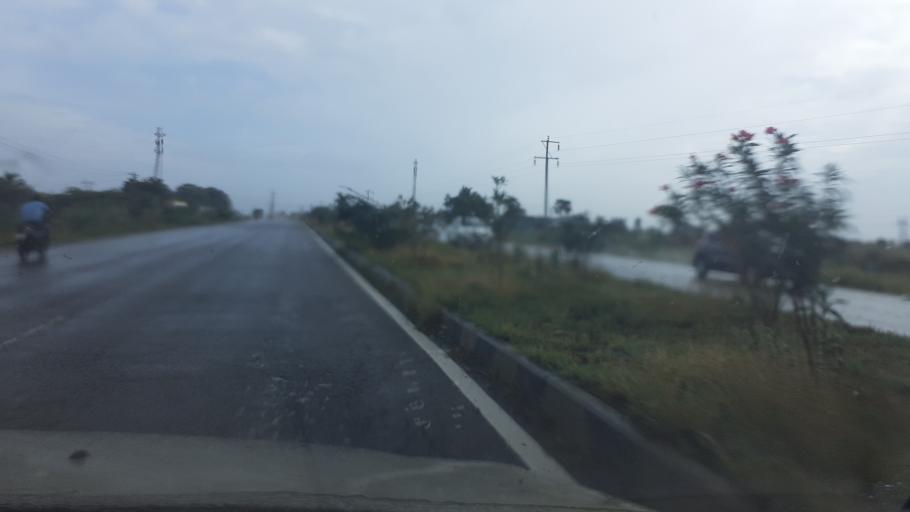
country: IN
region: Tamil Nadu
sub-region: Tirunelveli Kattabo
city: Gangaikondan
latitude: 8.9002
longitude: 77.7648
